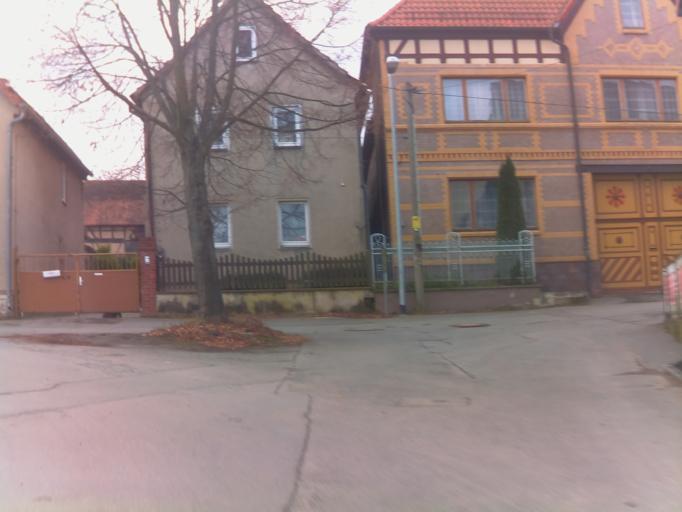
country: DE
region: Thuringia
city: Lemnitz
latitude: 50.7163
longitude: 11.8458
